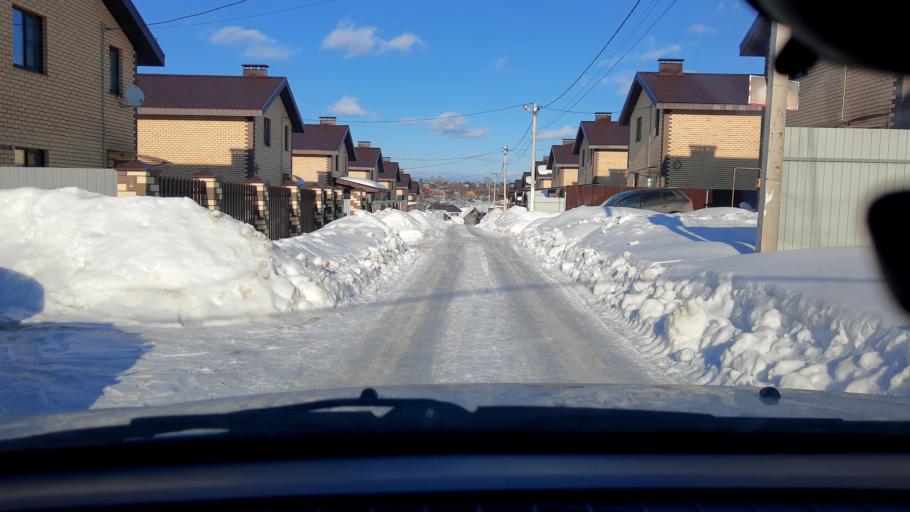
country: RU
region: Nizjnij Novgorod
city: Burevestnik
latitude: 56.1648
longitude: 43.7736
